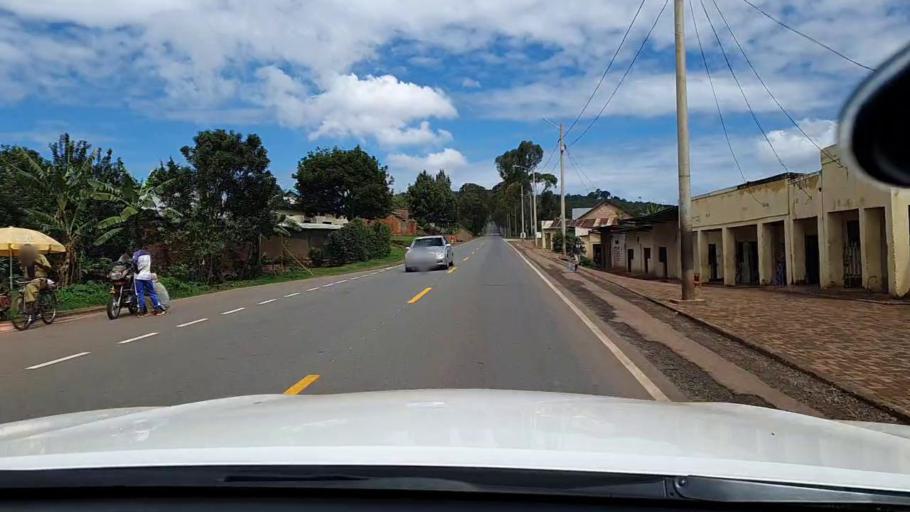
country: RW
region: Kigali
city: Kigali
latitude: -1.8363
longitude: 29.9527
